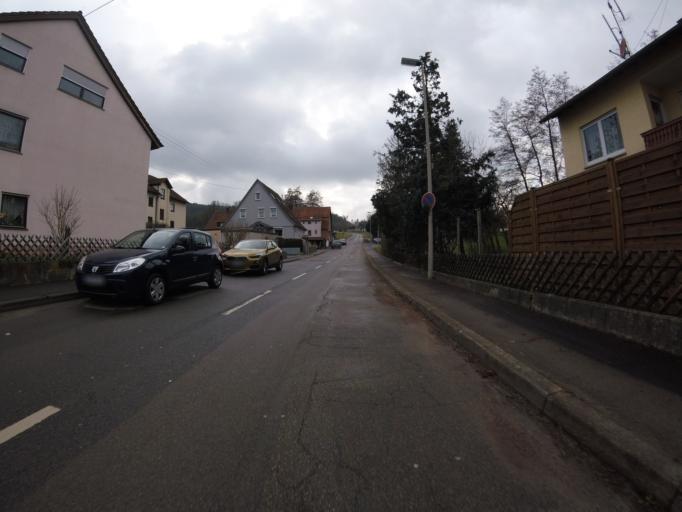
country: DE
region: Baden-Wuerttemberg
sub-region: Regierungsbezirk Stuttgart
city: Allmersbach im Tal
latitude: 48.9048
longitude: 9.4837
